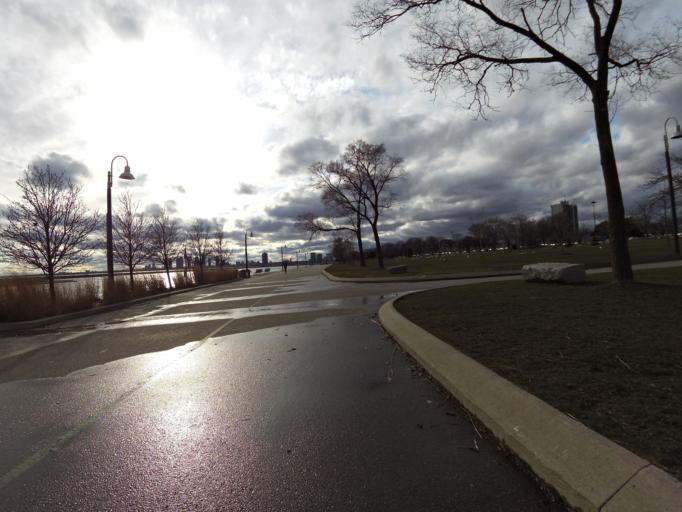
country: CA
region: Ontario
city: Toronto
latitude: 43.6301
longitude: -79.4289
